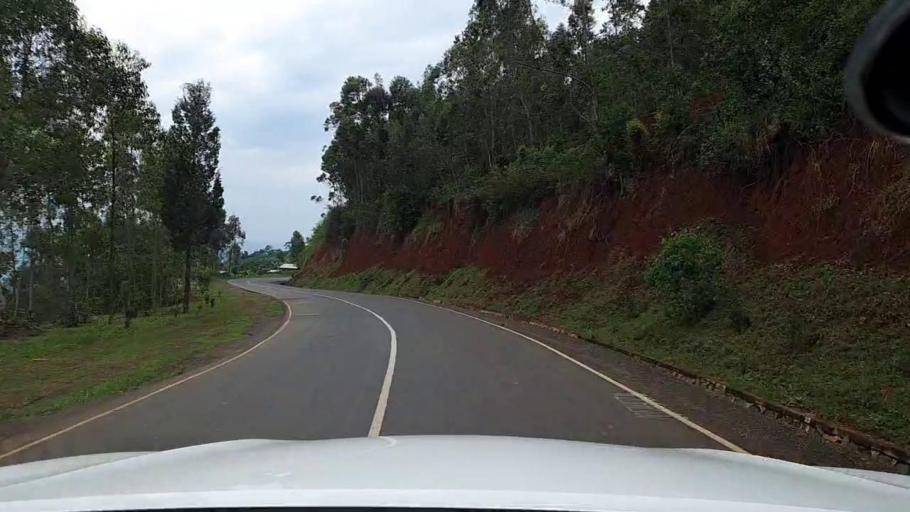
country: RW
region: Western Province
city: Cyangugu
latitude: -2.6486
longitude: 28.9660
